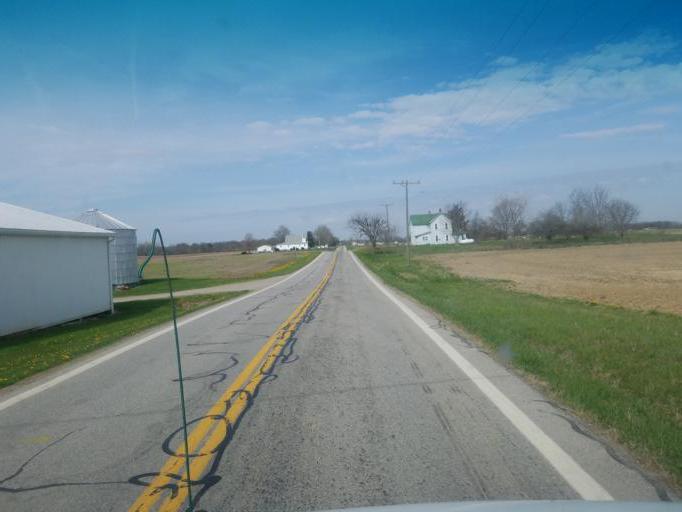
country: US
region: Ohio
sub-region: Union County
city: Richwood
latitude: 40.4839
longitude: -83.3814
